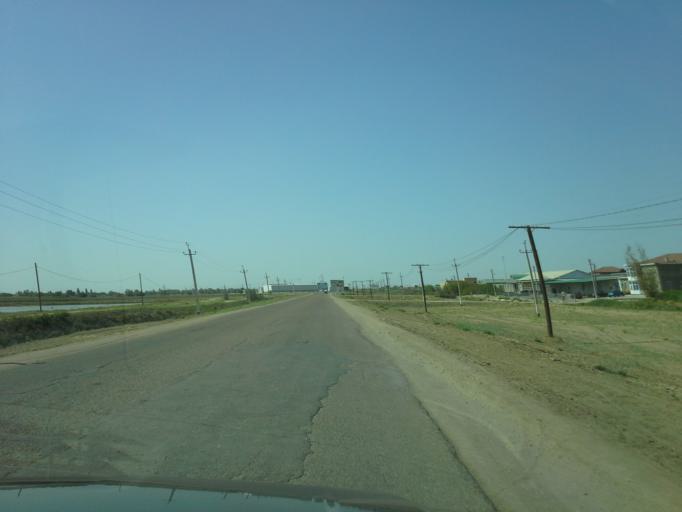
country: TM
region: Dasoguz
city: Dasoguz
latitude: 41.8058
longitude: 60.0086
